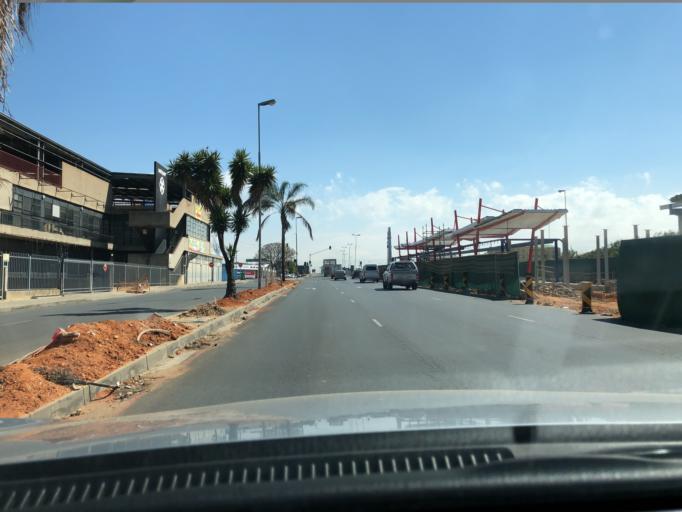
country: ZA
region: Gauteng
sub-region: City of Johannesburg Metropolitan Municipality
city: Modderfontein
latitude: -26.0980
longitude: 28.0855
